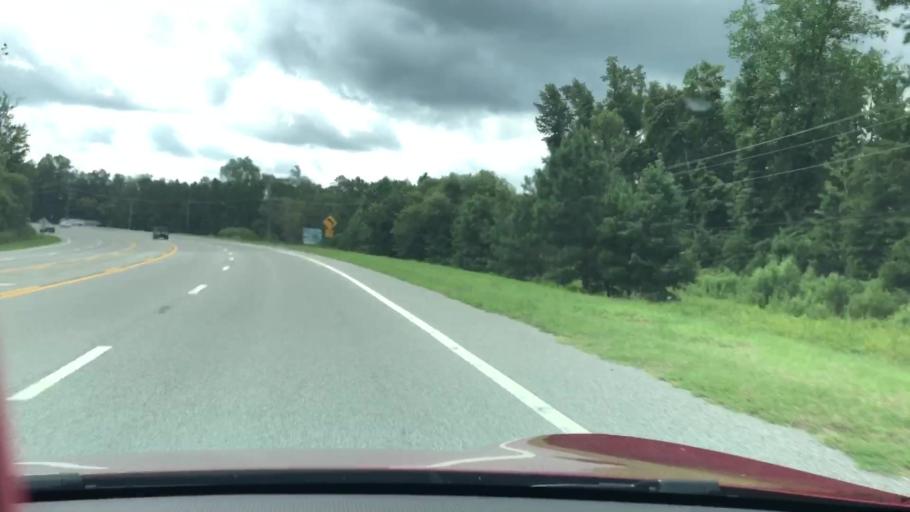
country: US
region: North Carolina
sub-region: Currituck County
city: Currituck
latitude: 36.4158
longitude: -76.0047
